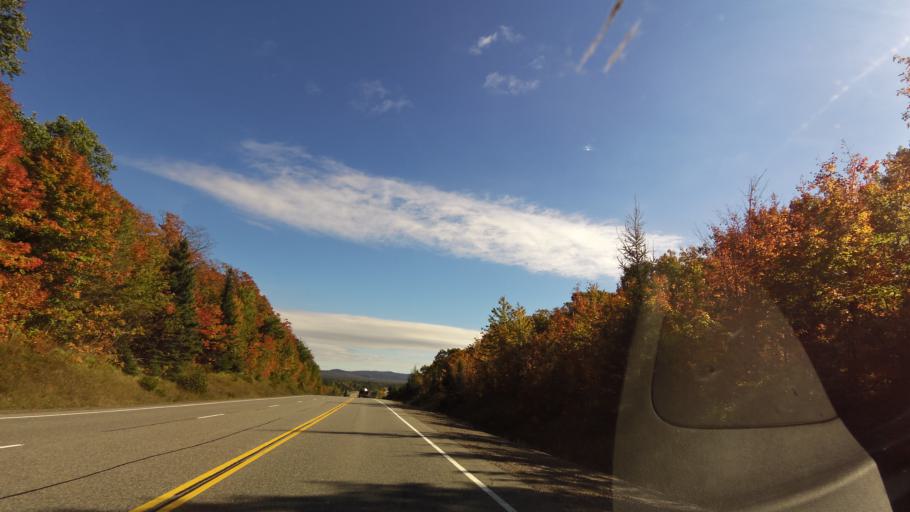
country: CA
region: Ontario
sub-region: Algoma
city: Sault Ste. Marie
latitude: 46.9449
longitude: -84.5898
